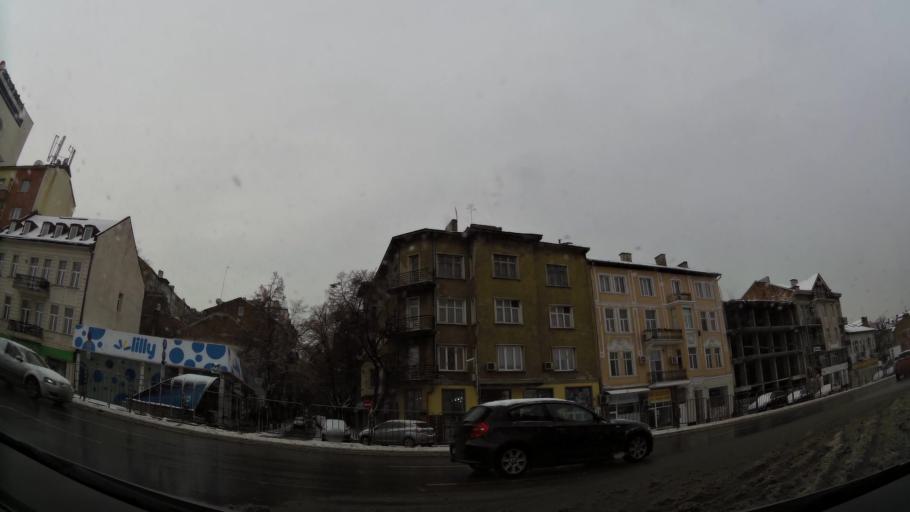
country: BG
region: Sofia-Capital
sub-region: Stolichna Obshtina
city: Sofia
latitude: 42.6983
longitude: 23.3193
